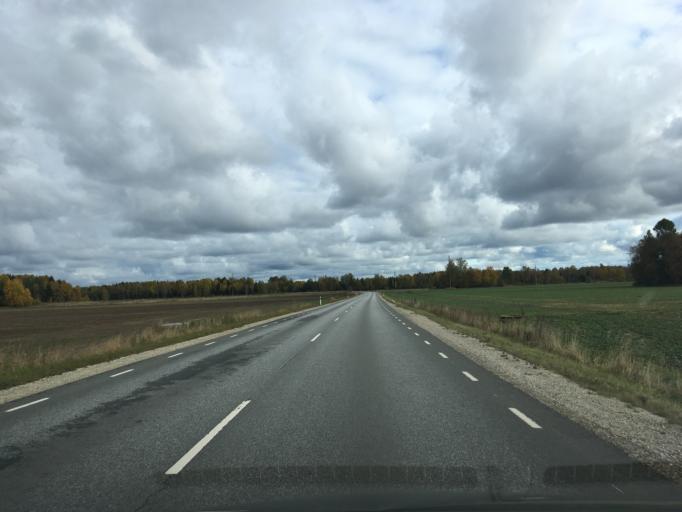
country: EE
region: Harju
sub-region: Anija vald
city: Kehra
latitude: 59.2596
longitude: 25.3420
